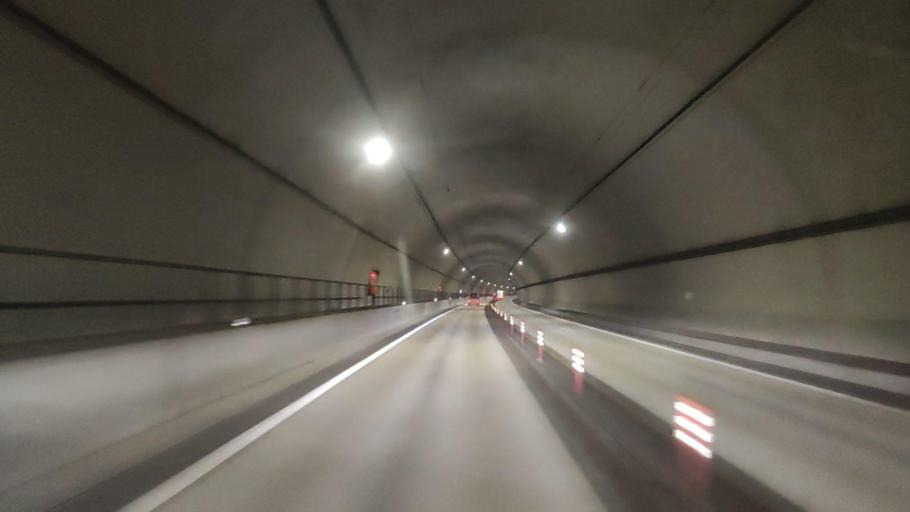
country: JP
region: Wakayama
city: Tanabe
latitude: 33.5903
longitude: 135.4403
